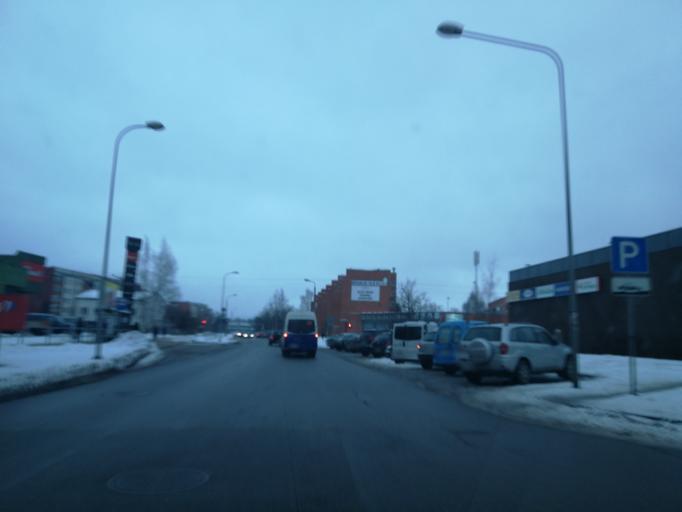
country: LV
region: Riga
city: Riga
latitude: 56.9453
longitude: 24.1721
